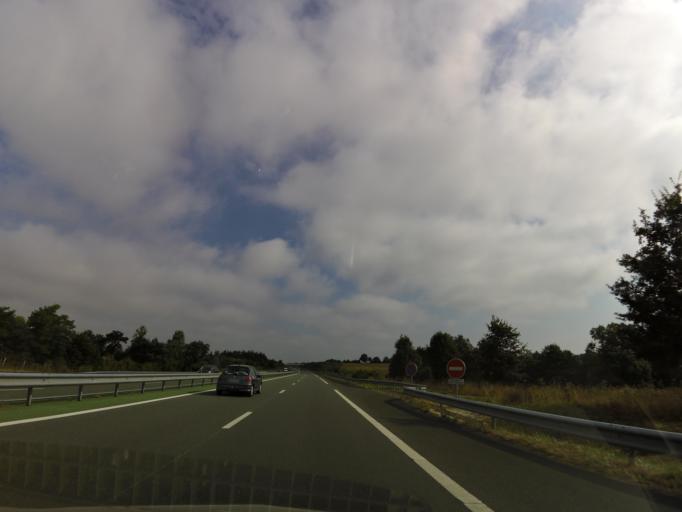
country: FR
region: Pays de la Loire
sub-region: Departement de la Vendee
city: La Ferriere
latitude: 46.7145
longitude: -1.2823
